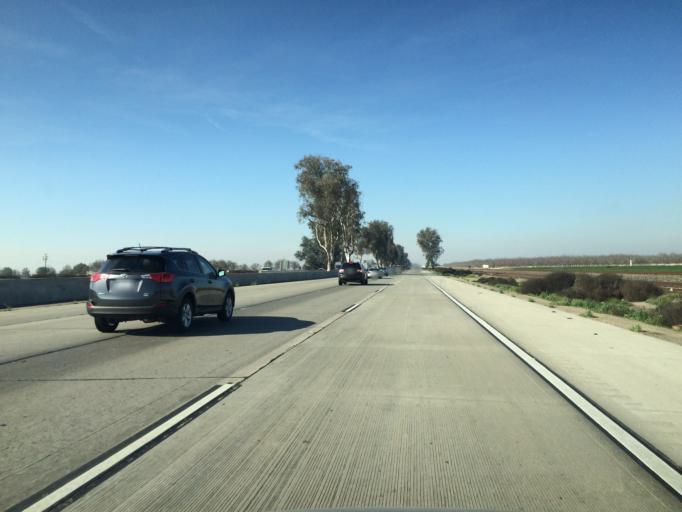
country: US
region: California
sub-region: Tulare County
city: Goshen
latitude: 36.3671
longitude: -119.4316
